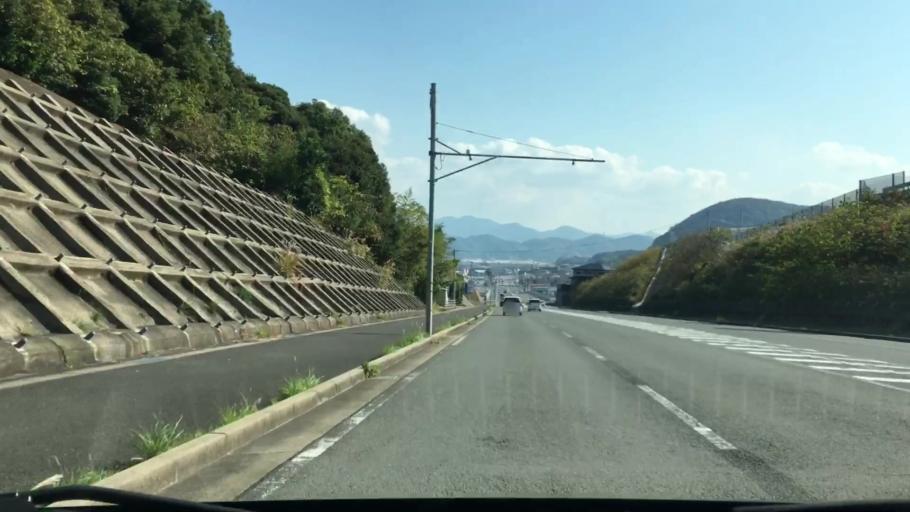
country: JP
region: Nagasaki
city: Togitsu
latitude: 32.8569
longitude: 129.8196
